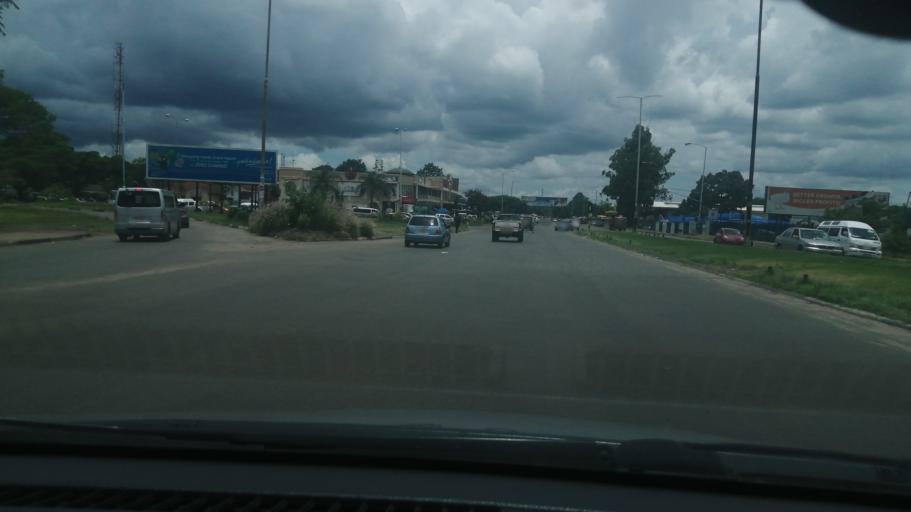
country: ZW
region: Harare
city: Harare
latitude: -17.8300
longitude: 31.0603
